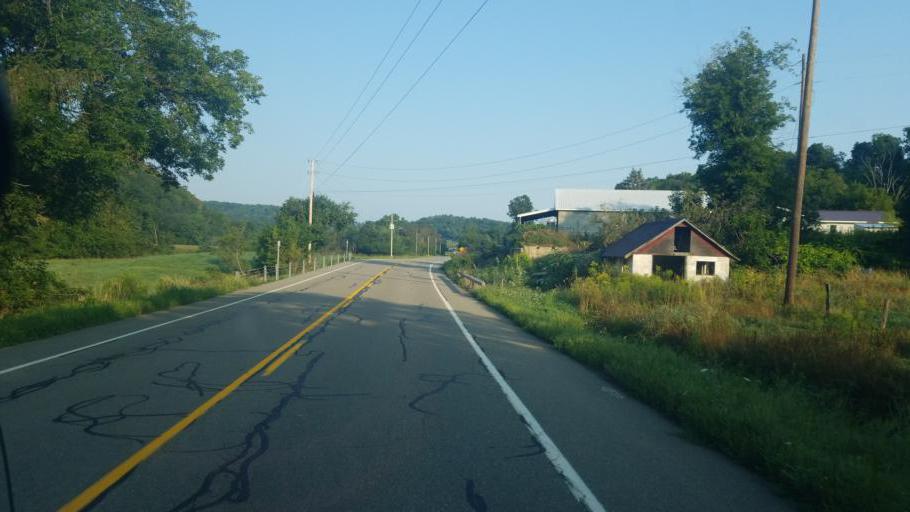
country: US
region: Pennsylvania
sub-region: Tioga County
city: Westfield
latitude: 42.0222
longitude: -77.5276
